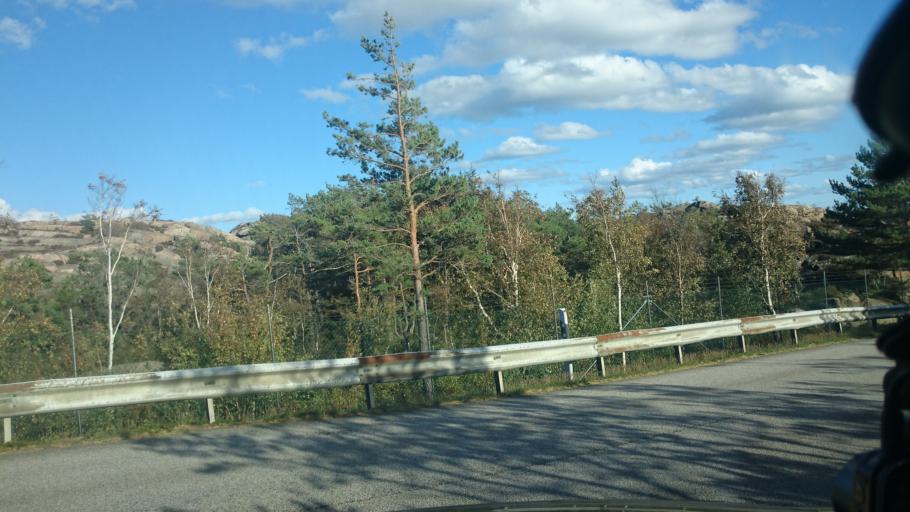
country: SE
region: Vaestra Goetaland
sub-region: Lysekils Kommun
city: Lysekil
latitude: 58.3387
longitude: 11.4155
